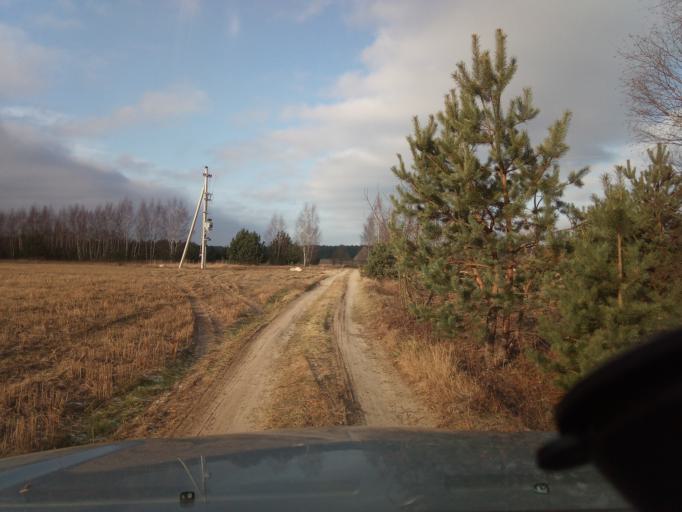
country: LT
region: Alytaus apskritis
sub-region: Alytaus rajonas
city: Daugai
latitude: 54.1140
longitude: 24.2381
